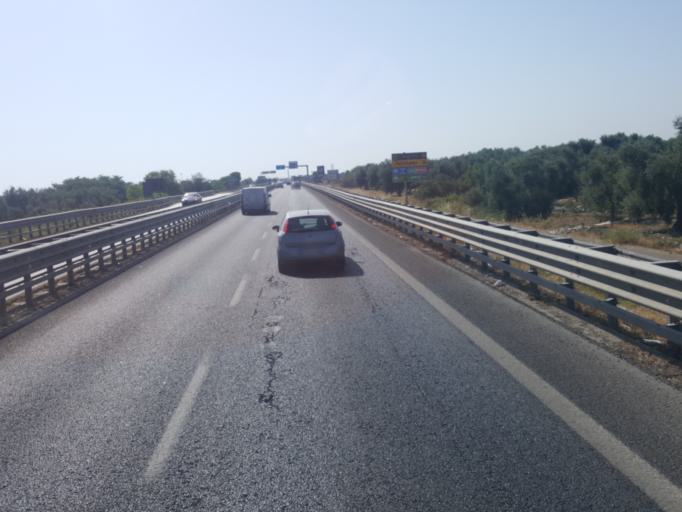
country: IT
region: Apulia
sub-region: Provincia di Barletta - Andria - Trani
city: Bisceglie
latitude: 41.2200
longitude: 16.5334
